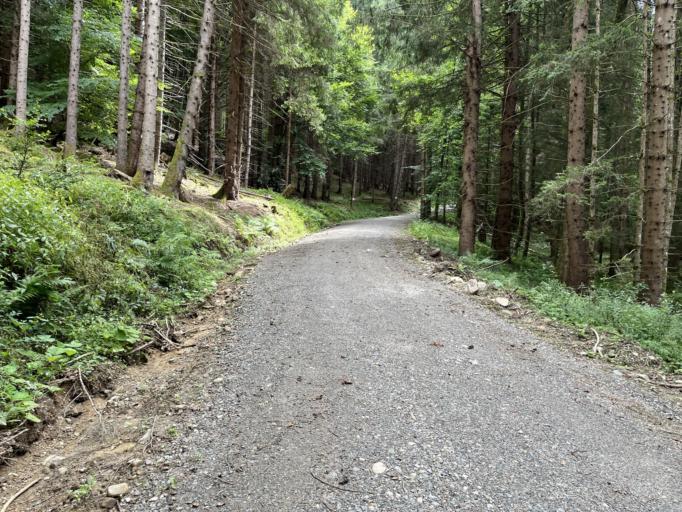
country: AT
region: Carinthia
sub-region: Politischer Bezirk Spittal an der Drau
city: Millstatt
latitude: 46.7926
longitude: 13.5498
